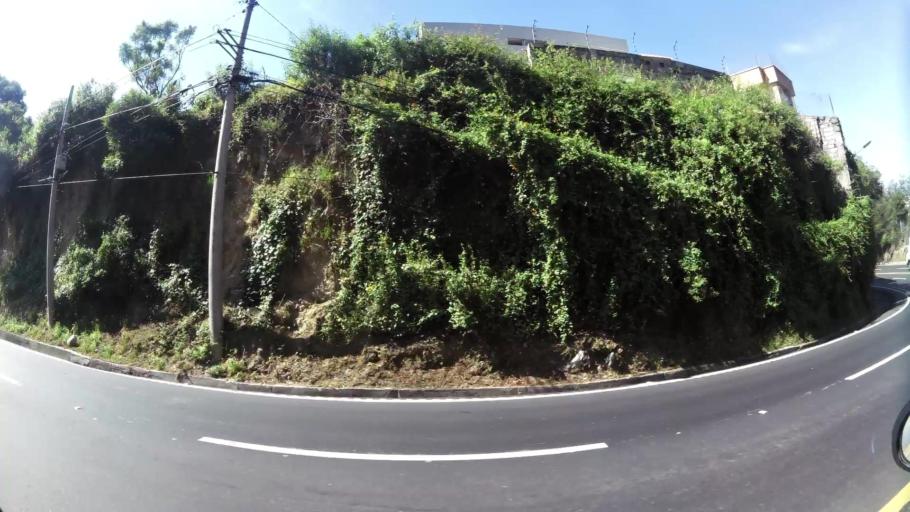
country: EC
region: Pichincha
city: Quito
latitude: -0.1898
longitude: -78.4462
